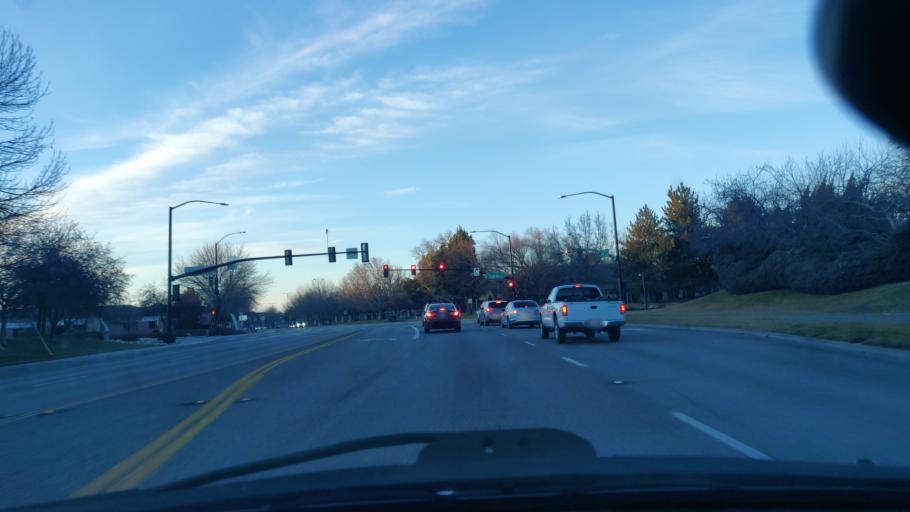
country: US
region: Idaho
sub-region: Ada County
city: Boise
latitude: 43.5888
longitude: -116.1739
